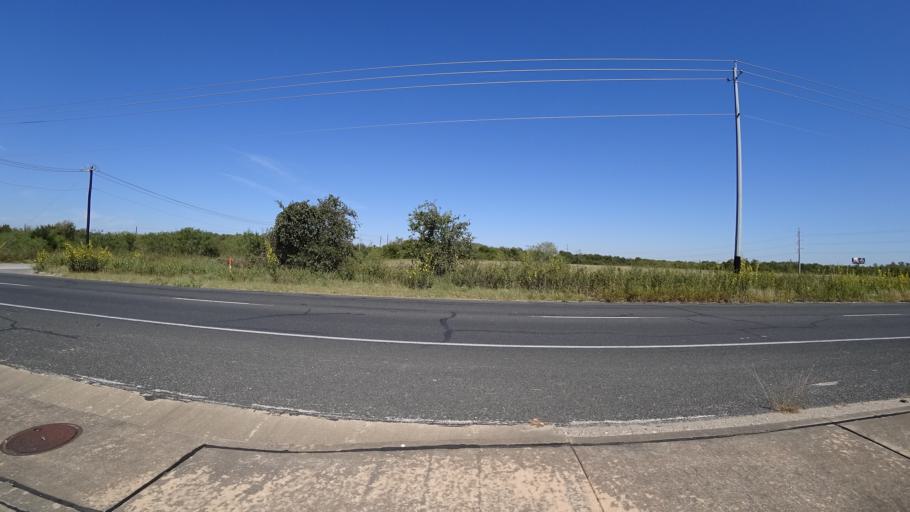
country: US
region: Texas
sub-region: Travis County
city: Austin
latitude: 30.1987
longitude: -97.6881
